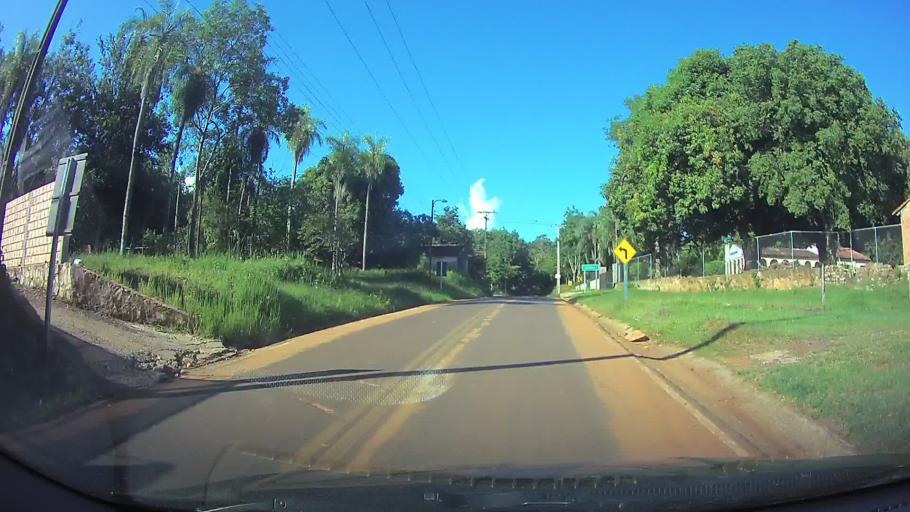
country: PY
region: Central
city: Itaugua
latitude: -25.3697
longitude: -57.3685
